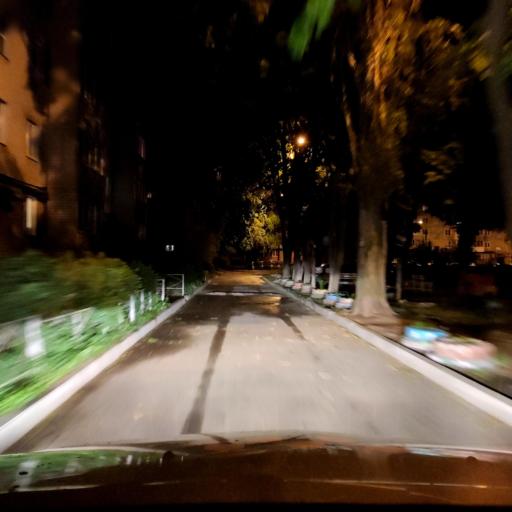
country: RU
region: Voronezj
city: Maslovka
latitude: 51.5884
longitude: 39.3213
